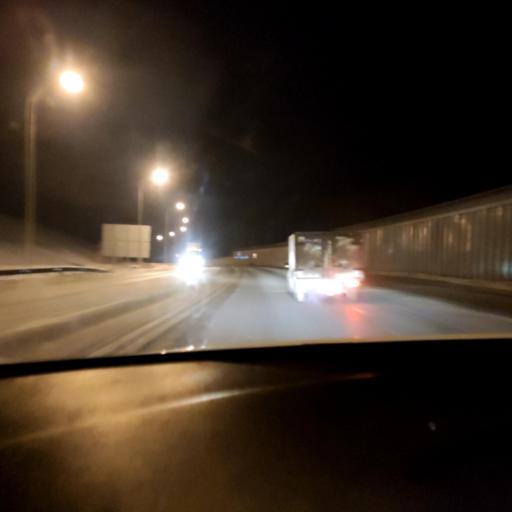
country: RU
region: Tatarstan
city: Aysha
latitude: 55.8744
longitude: 48.6601
